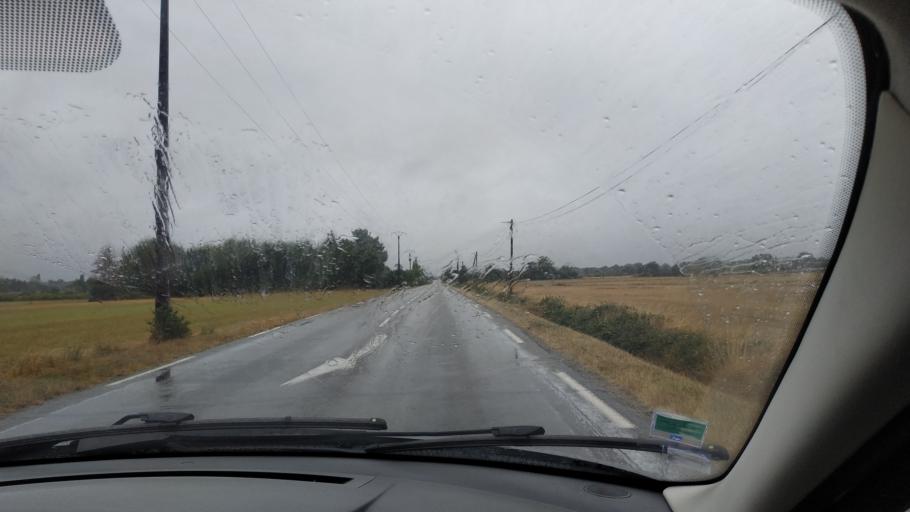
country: FR
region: Centre
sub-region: Departement du Loiret
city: Bellegarde
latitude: 47.9234
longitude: 2.3955
